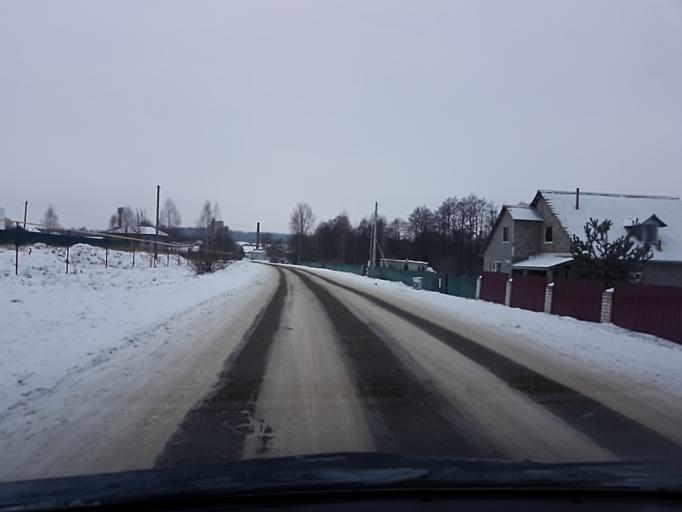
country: BY
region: Minsk
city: Rakaw
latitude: 53.9562
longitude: 27.0562
